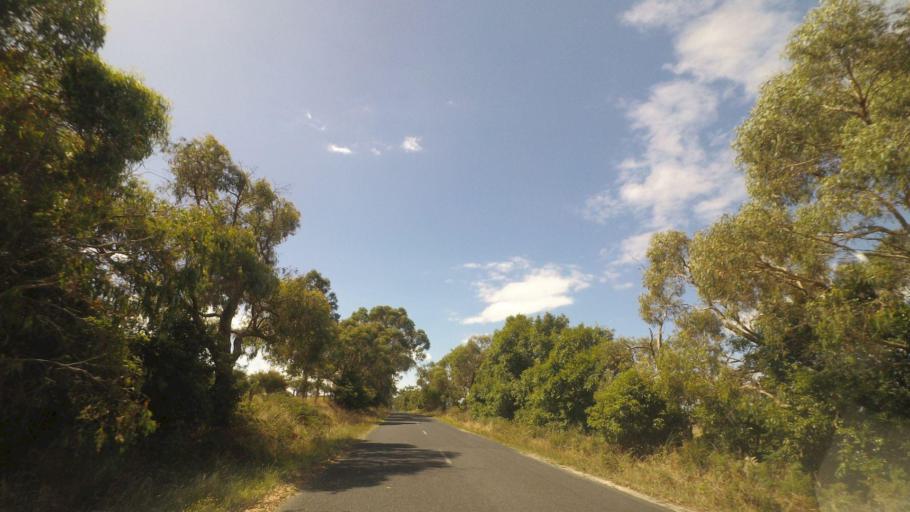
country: AU
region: Victoria
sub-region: Cardinia
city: Koo-Wee-Rup
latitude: -38.3152
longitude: 145.6664
